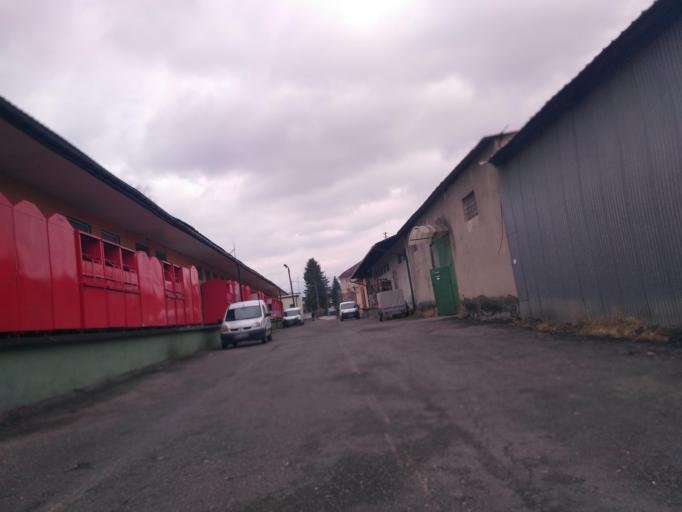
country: PL
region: Subcarpathian Voivodeship
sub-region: Powiat strzyzowski
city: Strzyzow
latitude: 49.8687
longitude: 21.8024
